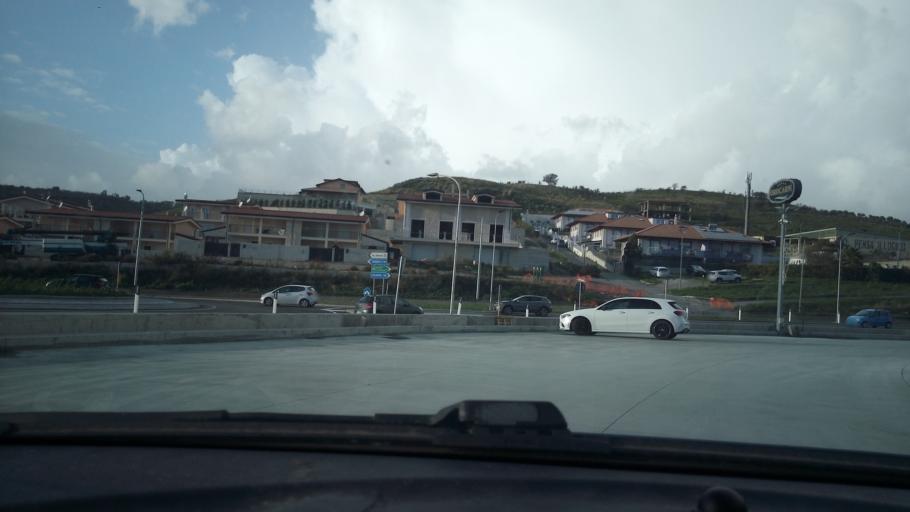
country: IT
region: Calabria
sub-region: Provincia di Catanzaro
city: Barone
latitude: 38.8351
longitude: 16.6369
